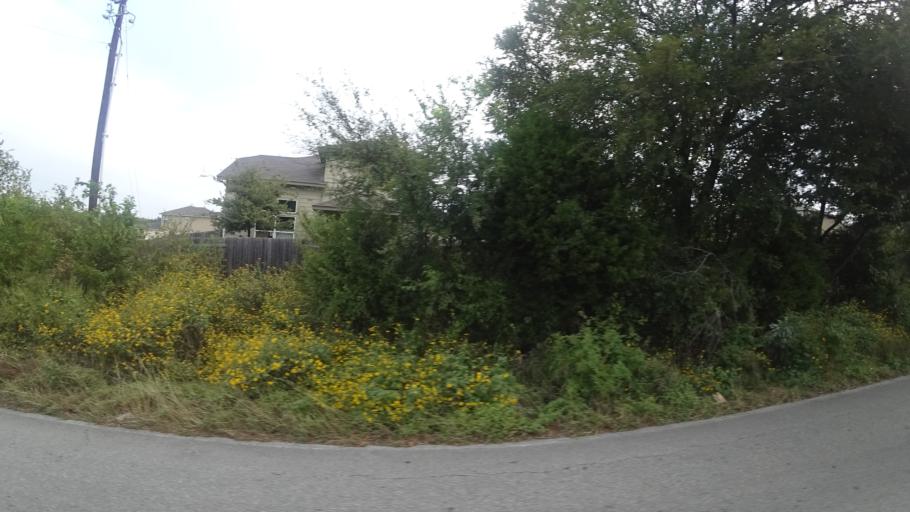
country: US
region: Texas
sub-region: Travis County
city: Pflugerville
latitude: 30.3669
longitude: -97.6542
